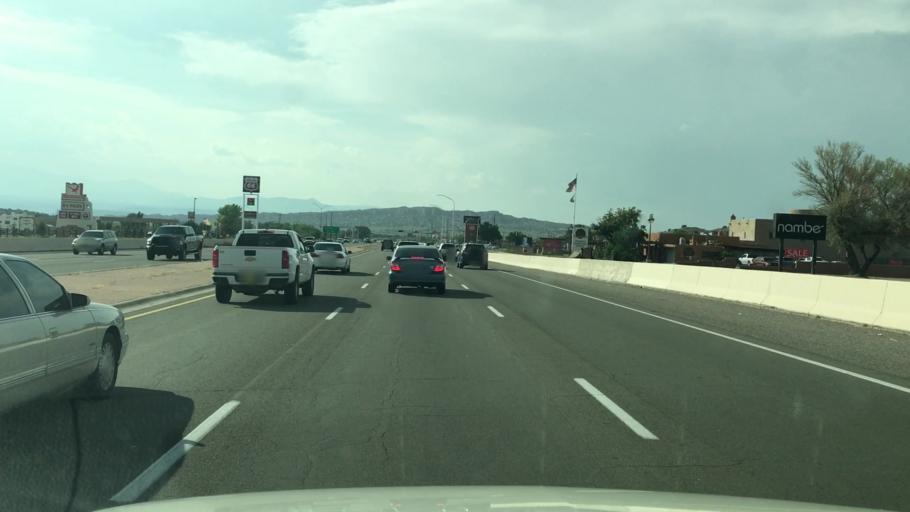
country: US
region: New Mexico
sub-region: Santa Fe County
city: Pojoaque
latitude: 35.8803
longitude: -106.0115
